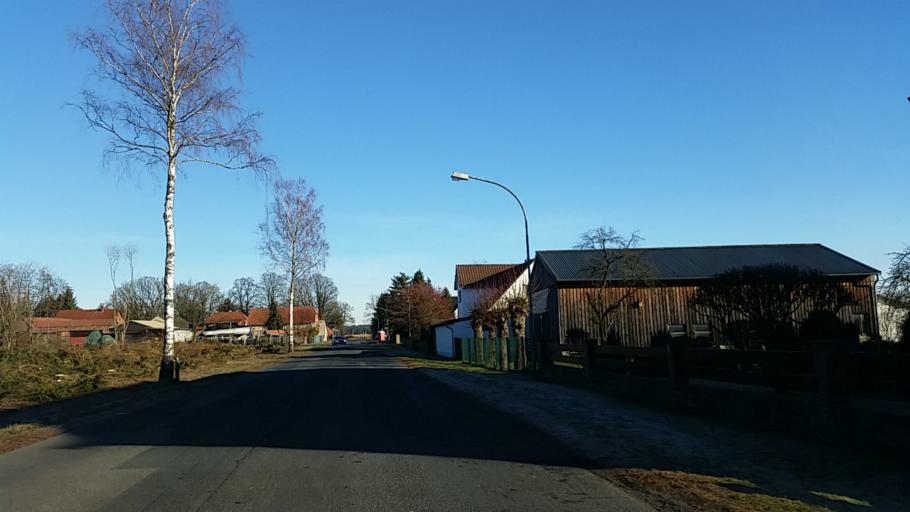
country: DE
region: Lower Saxony
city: Sassenburg
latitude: 52.5521
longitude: 10.6793
